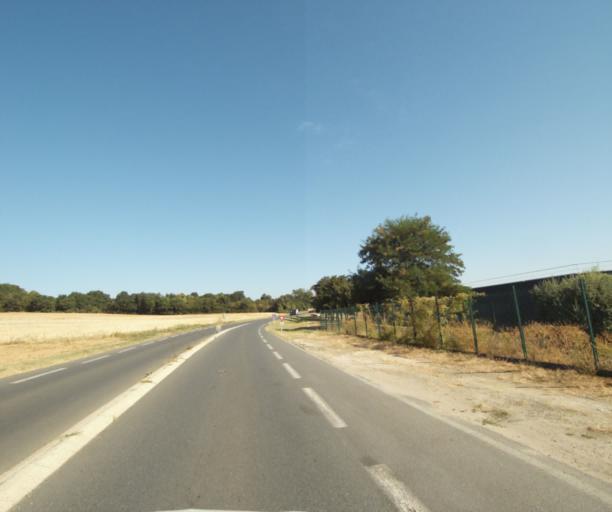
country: FR
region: Ile-de-France
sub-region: Departement de l'Essonne
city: Baulne
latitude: 48.4991
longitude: 2.3490
